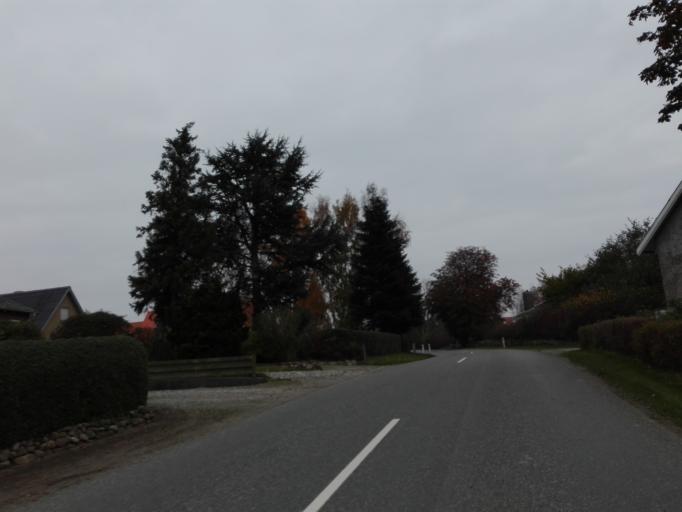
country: DK
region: Central Jutland
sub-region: Arhus Kommune
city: Beder
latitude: 56.0457
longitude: 10.2403
